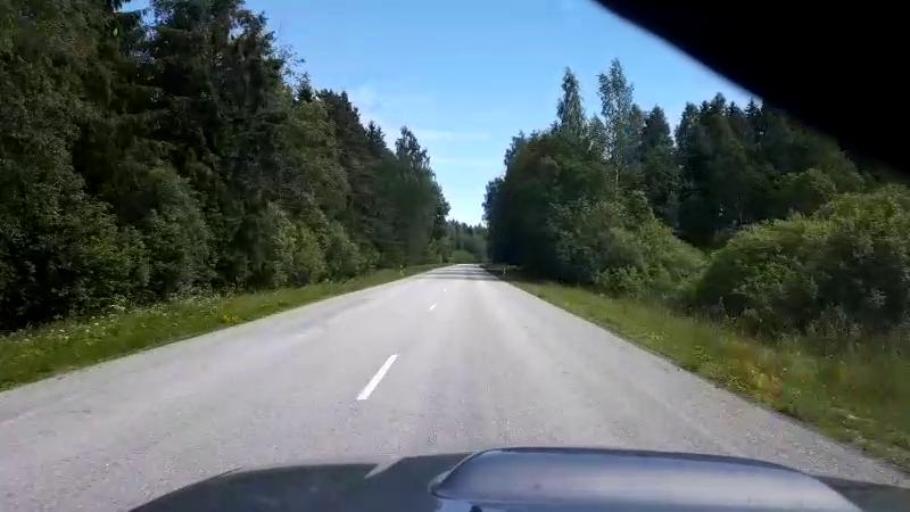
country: EE
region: Laeaene-Virumaa
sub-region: Rakke vald
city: Rakke
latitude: 58.9144
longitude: 26.2658
